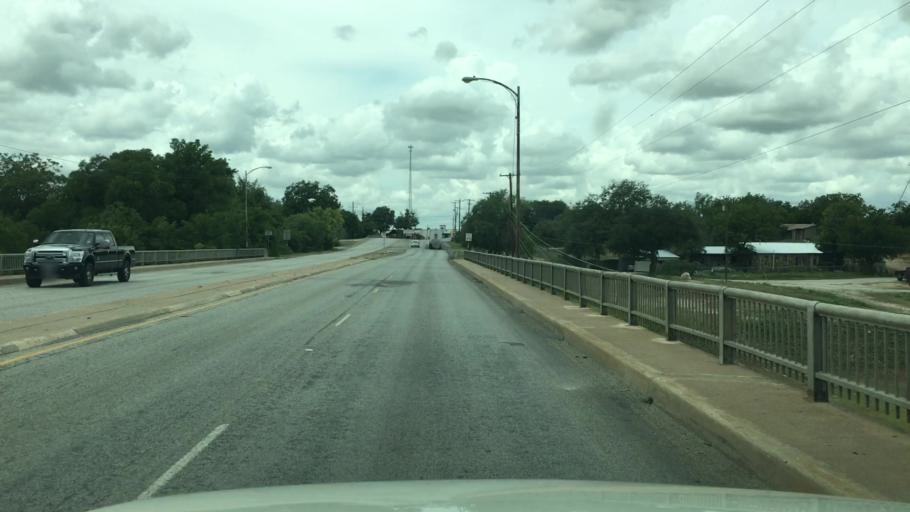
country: US
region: Texas
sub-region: McCulloch County
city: Brady
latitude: 31.1359
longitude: -99.3423
